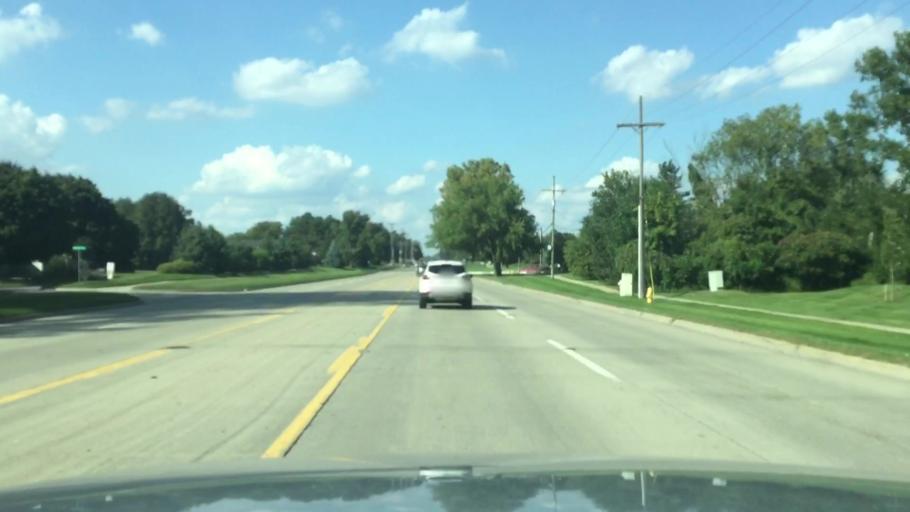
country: US
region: Michigan
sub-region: Wayne County
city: Westland
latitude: 42.3414
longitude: -83.4094
